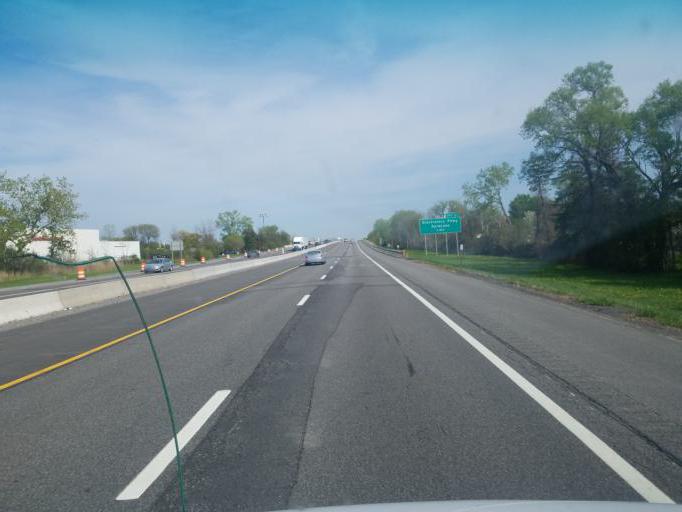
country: US
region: New York
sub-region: Onondaga County
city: Liverpool
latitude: 43.1114
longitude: -76.2031
